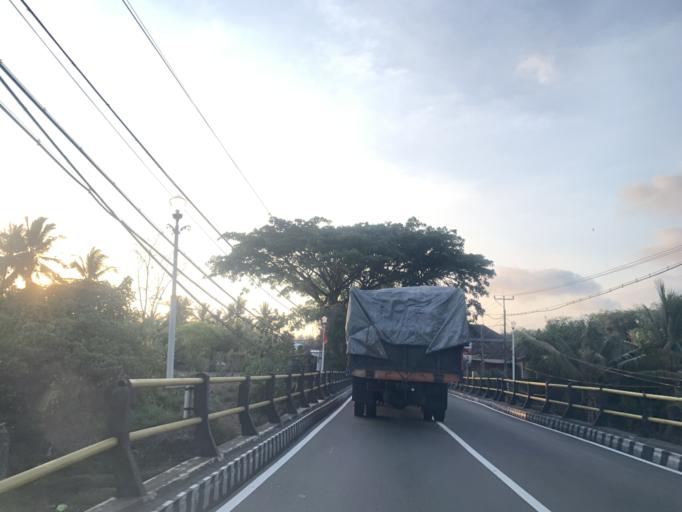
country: ID
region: Bali
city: Banjar Swastika
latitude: -8.4315
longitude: 114.8531
